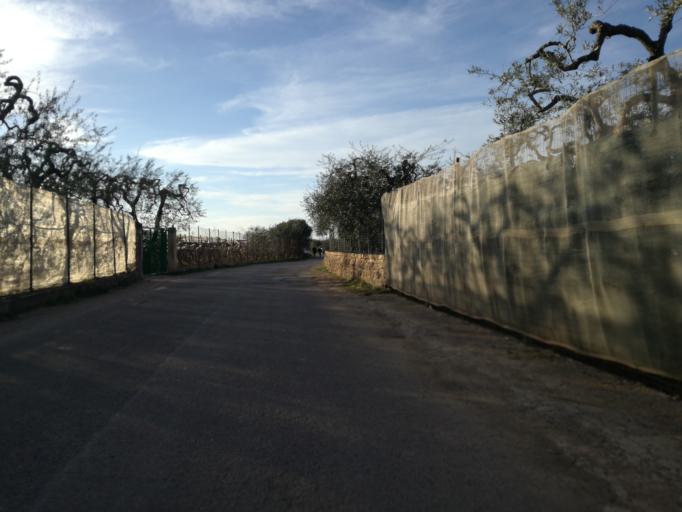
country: IT
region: Apulia
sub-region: Provincia di Bari
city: Valenzano
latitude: 41.0511
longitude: 16.9001
